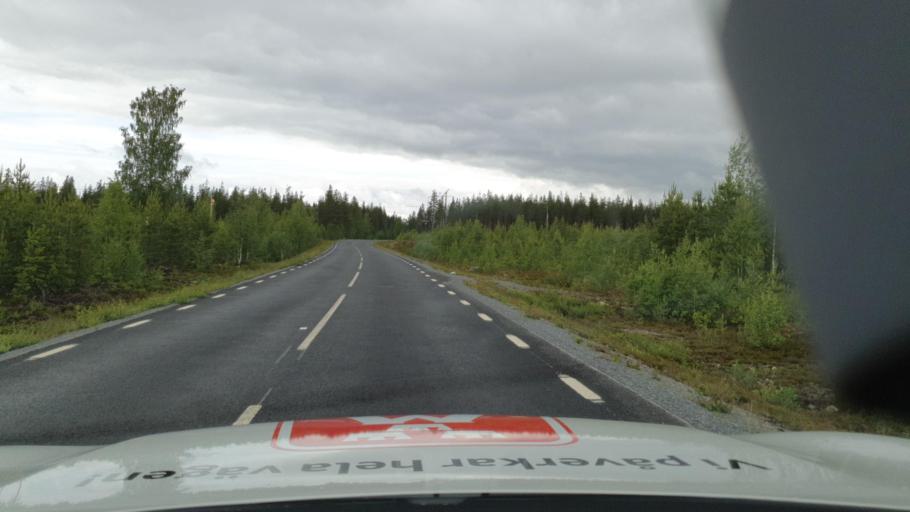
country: SE
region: Vaesterbotten
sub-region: Dorotea Kommun
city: Dorotea
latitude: 64.1984
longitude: 16.5751
